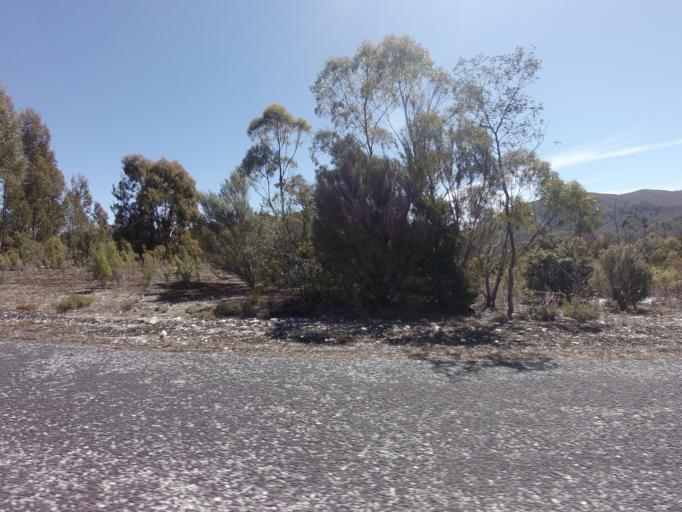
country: AU
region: Tasmania
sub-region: Huon Valley
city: Geeveston
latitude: -42.8078
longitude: 146.0972
